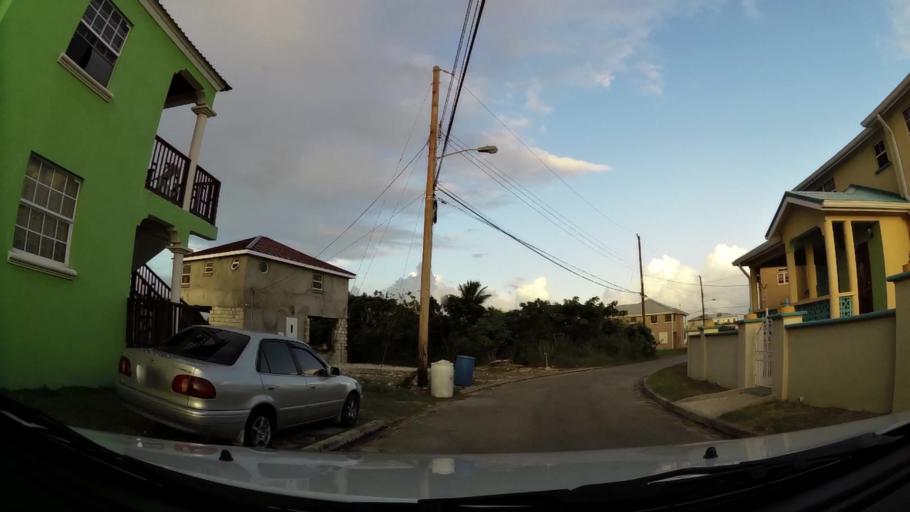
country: BB
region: Saint Philip
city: Crane
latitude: 13.1030
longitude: -59.4686
